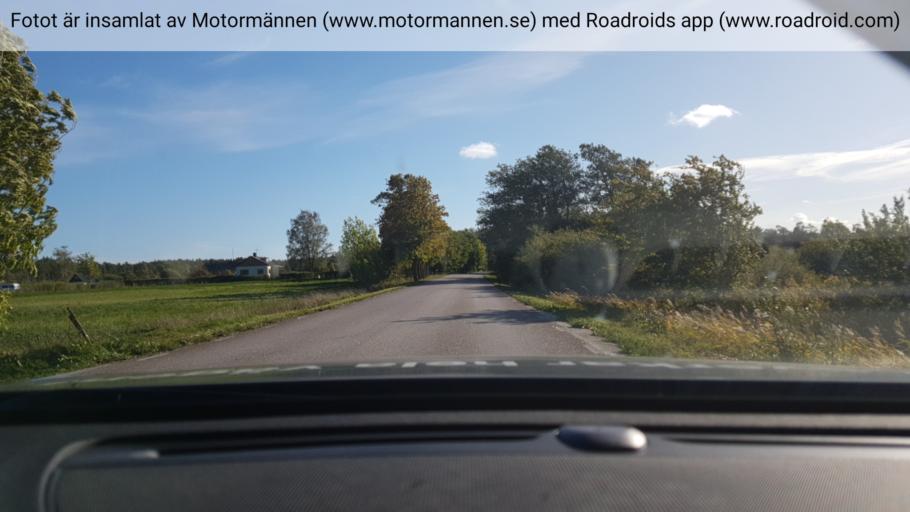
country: SE
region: Gotland
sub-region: Gotland
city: Slite
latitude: 57.8320
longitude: 18.8028
